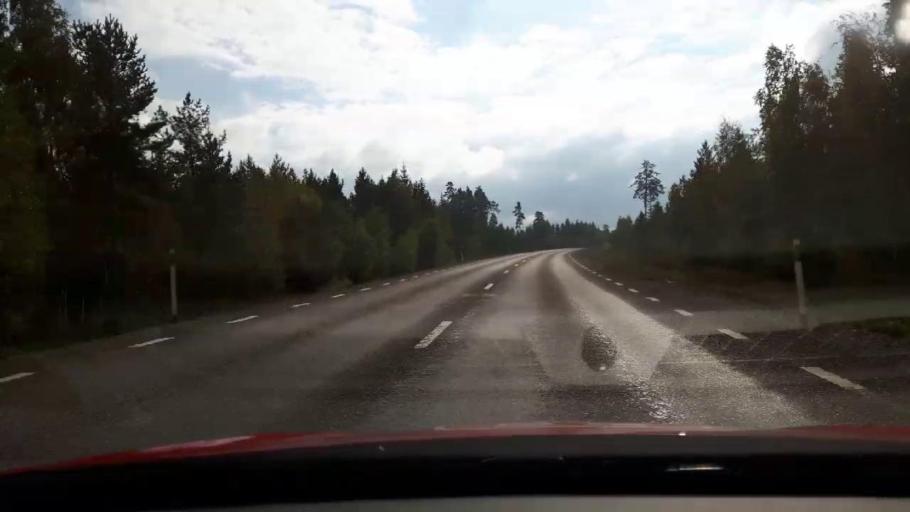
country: SE
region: Gaevleborg
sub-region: Gavle Kommun
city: Norrsundet
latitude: 61.0794
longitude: 16.9625
